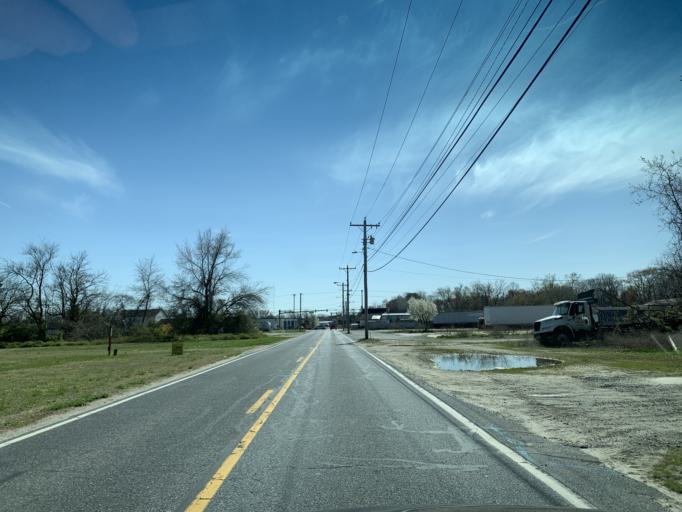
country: US
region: Delaware
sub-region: Sussex County
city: Milford
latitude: 38.9202
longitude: -75.4181
